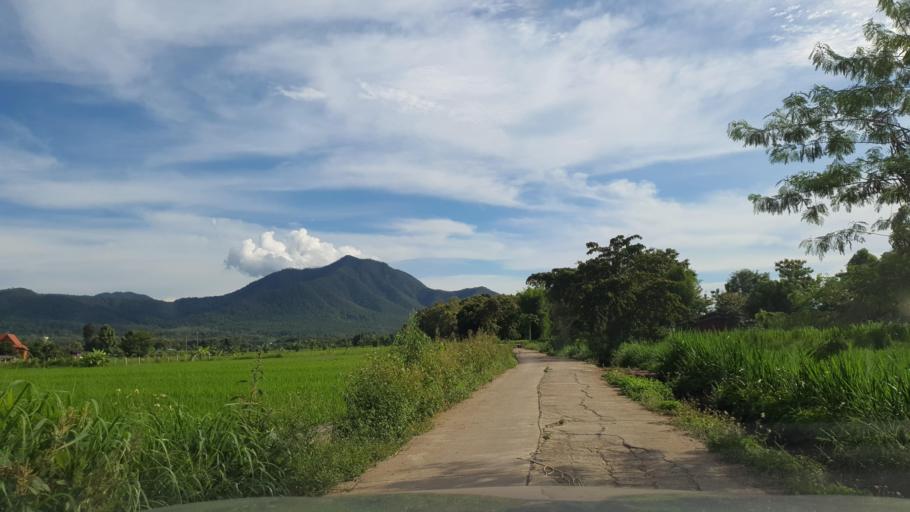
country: TH
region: Chiang Mai
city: Mae On
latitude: 18.7659
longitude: 99.2561
